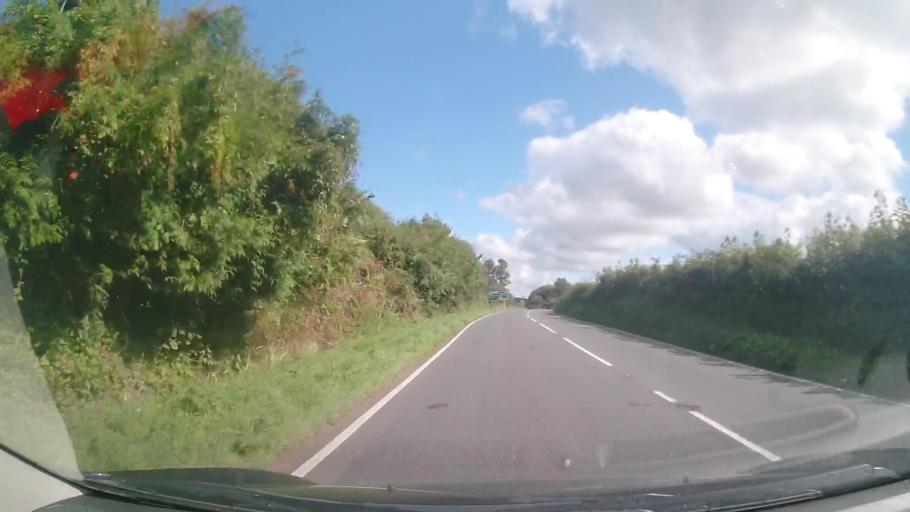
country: GB
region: Wales
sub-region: Pembrokeshire
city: Pembroke
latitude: 51.6883
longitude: -4.8690
